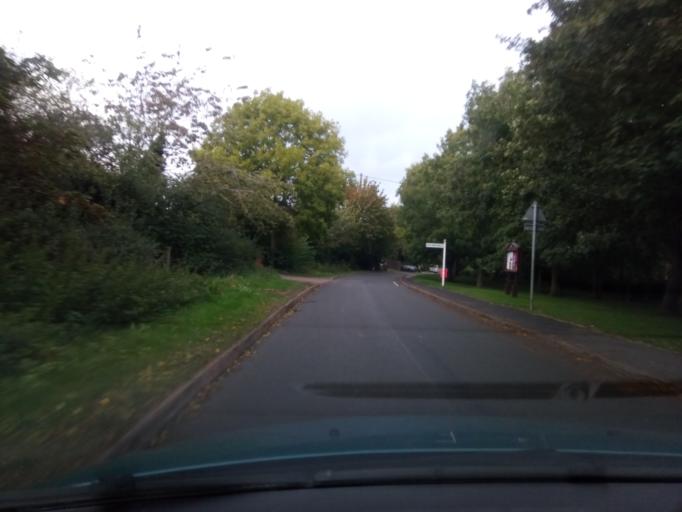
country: GB
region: England
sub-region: Leicestershire
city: Sileby
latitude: 52.7530
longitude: -1.0881
